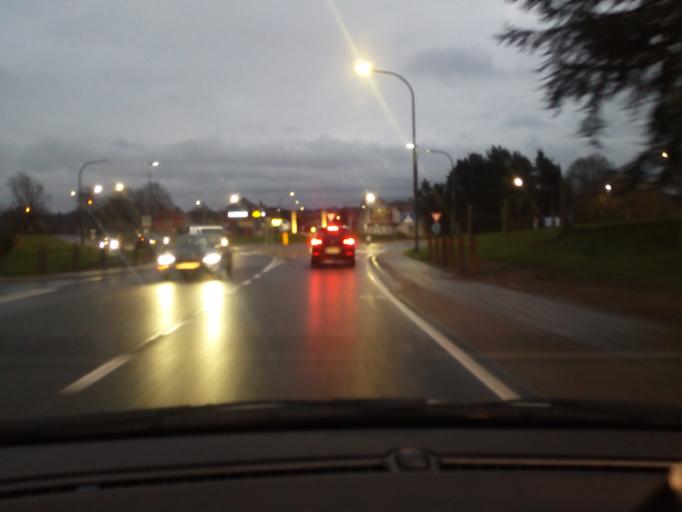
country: BE
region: Wallonia
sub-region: Province du Hainaut
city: Binche
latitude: 50.4160
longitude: 4.1475
